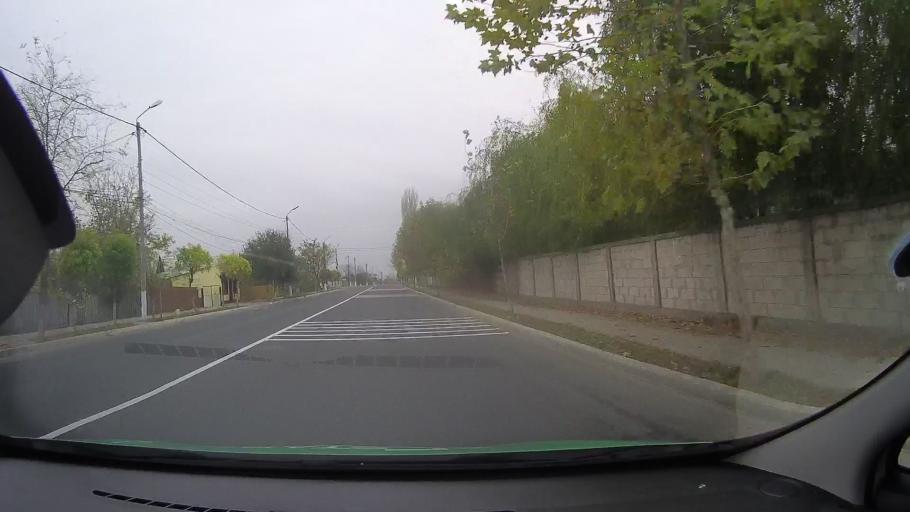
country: RO
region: Constanta
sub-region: Oras Harsova
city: Harsova
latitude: 44.6895
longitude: 27.9584
